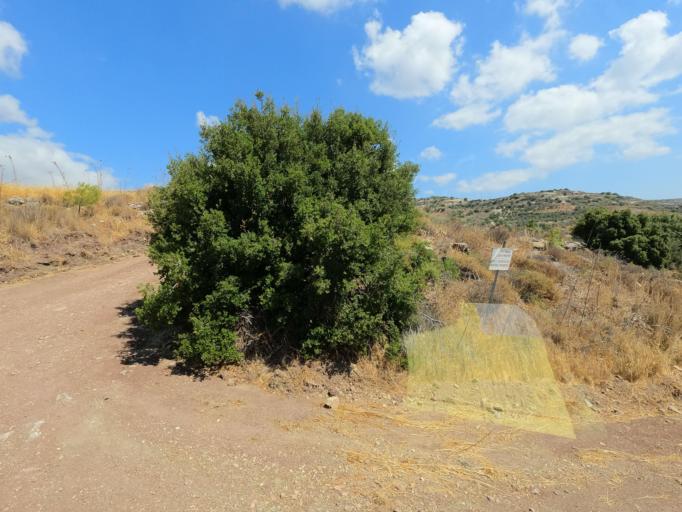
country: CY
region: Limassol
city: Pachna
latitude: 34.7930
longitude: 32.6859
